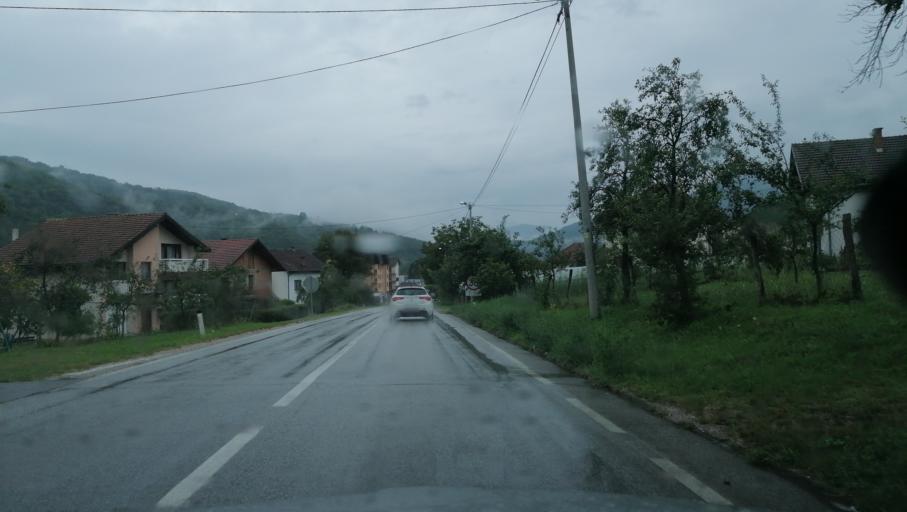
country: BA
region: Federation of Bosnia and Herzegovina
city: Gorazde
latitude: 43.6780
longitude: 19.0291
